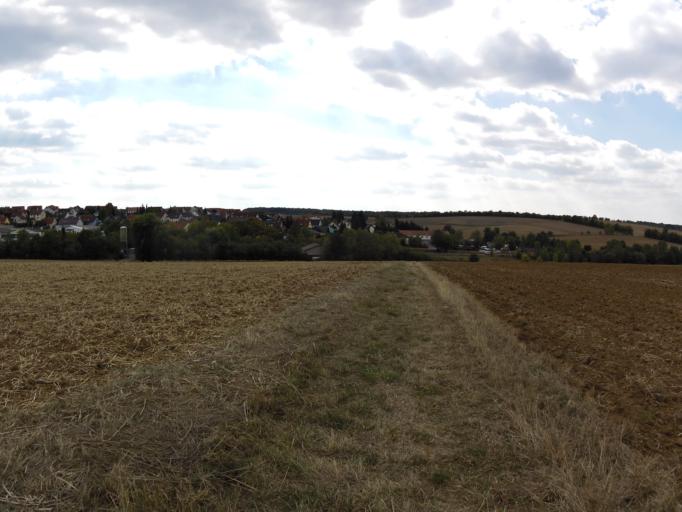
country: DE
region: Bavaria
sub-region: Regierungsbezirk Unterfranken
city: Waldbuttelbrunn
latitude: 49.7892
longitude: 9.8301
